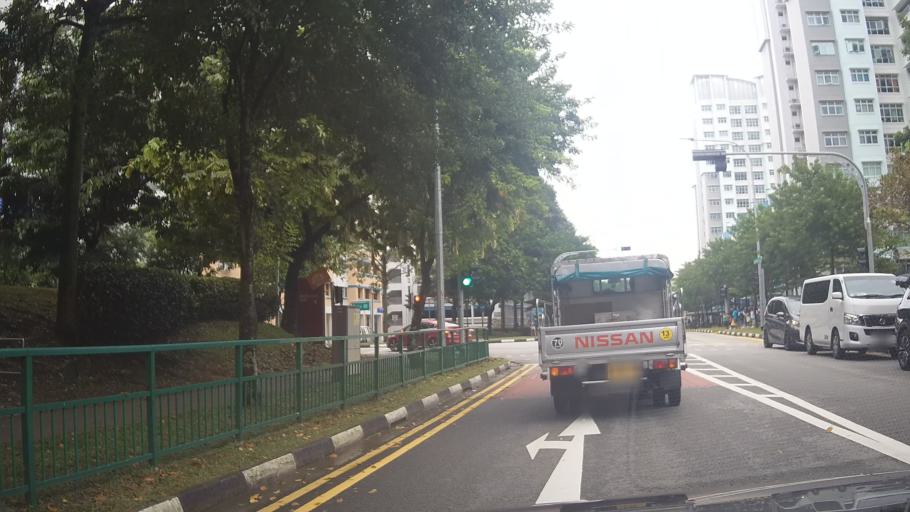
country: MY
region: Johor
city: Johor Bahru
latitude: 1.4472
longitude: 103.8011
